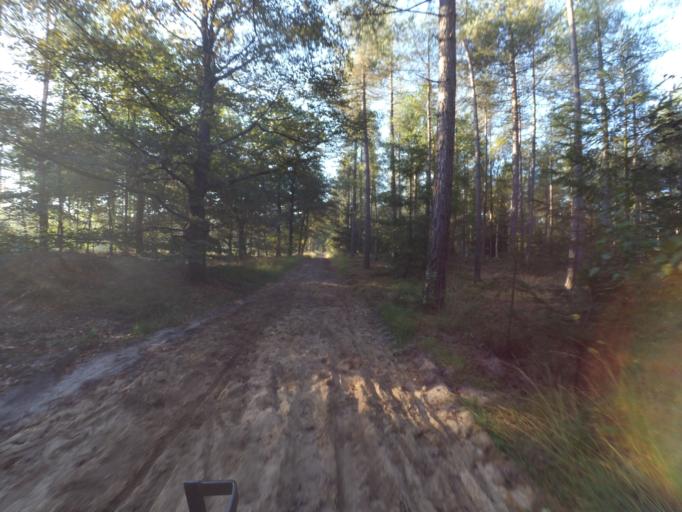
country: NL
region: Utrecht
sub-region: Gemeente Utrechtse Heuvelrug
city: Maarn
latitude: 52.0879
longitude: 5.3709
